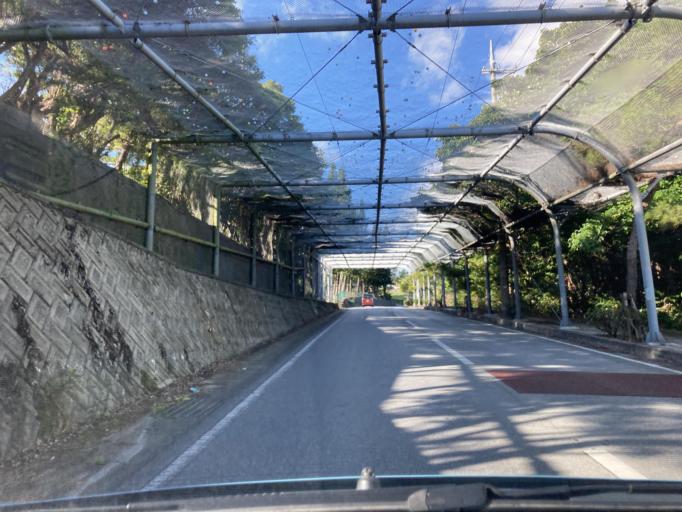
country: JP
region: Okinawa
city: Ginowan
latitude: 26.2156
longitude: 127.7501
